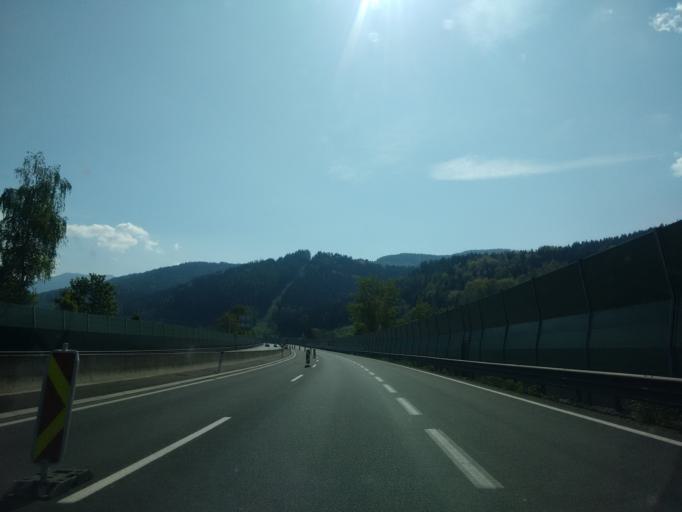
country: AT
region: Styria
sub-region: Politischer Bezirk Bruck-Muerzzuschlag
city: Oberaich
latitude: 47.3981
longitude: 15.2294
